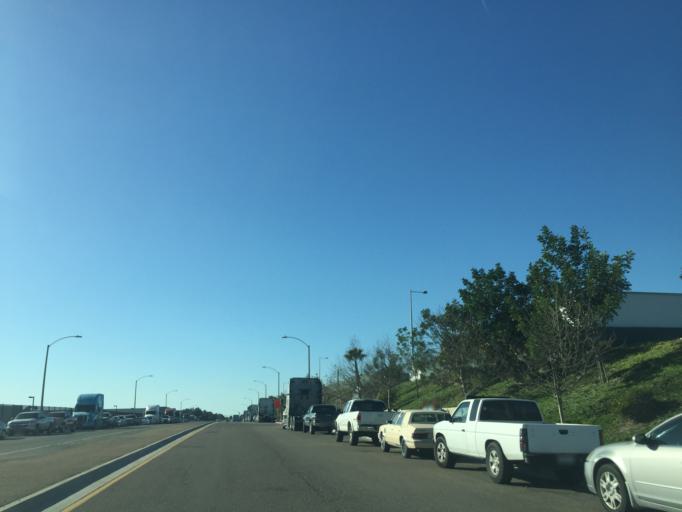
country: MX
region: Baja California
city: Tijuana
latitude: 32.5601
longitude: -116.9238
